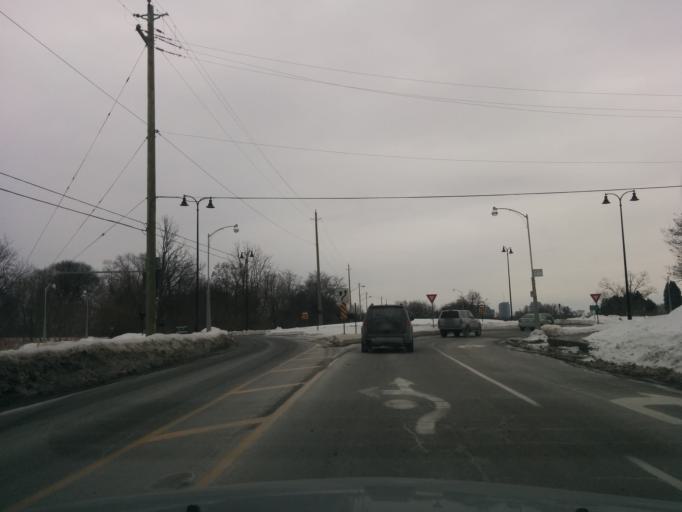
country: CA
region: Ontario
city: Ottawa
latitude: 45.3910
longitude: -75.7076
